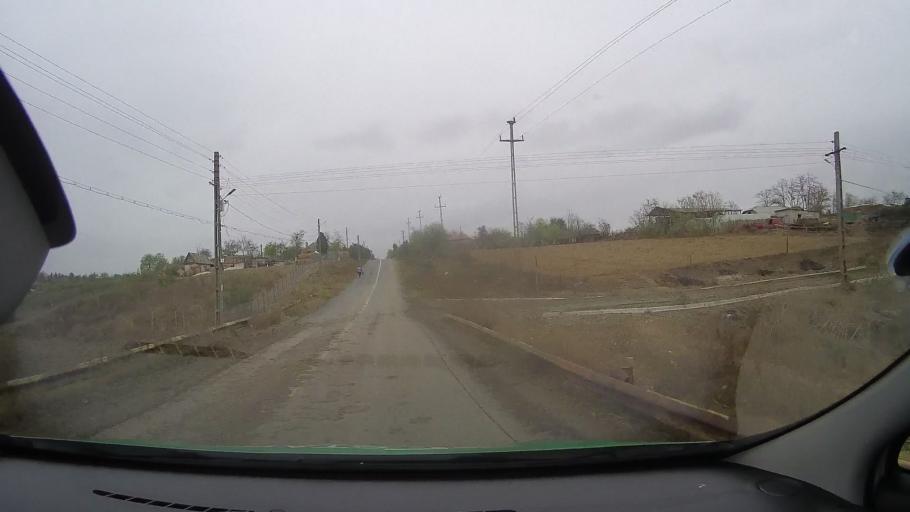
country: RO
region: Constanta
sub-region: Comuna Pantelimon
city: Pantelimon
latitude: 44.5426
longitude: 28.3291
